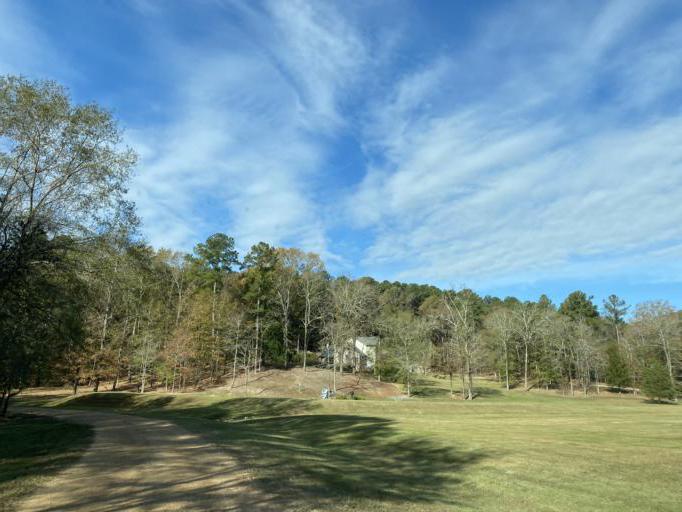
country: US
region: Mississippi
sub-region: Madison County
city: Ridgeland
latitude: 32.4620
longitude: -90.1907
